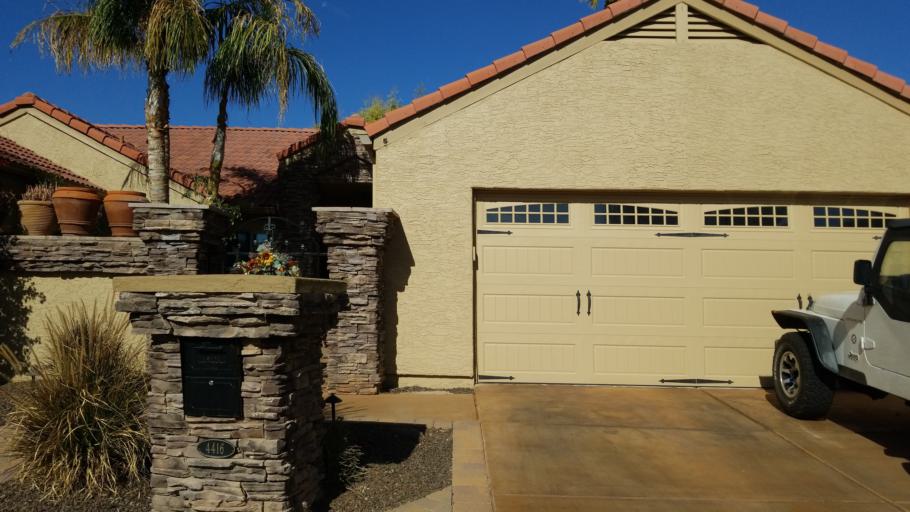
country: US
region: Arizona
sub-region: Maricopa County
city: Paradise Valley
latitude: 33.5915
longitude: -111.9857
